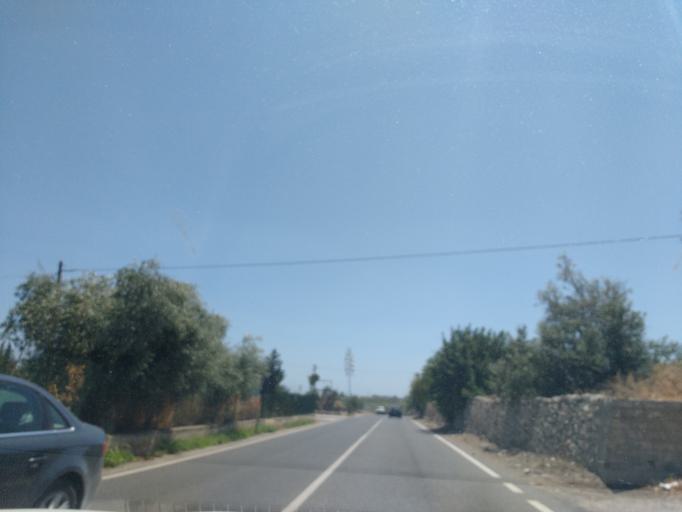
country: IT
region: Sicily
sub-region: Provincia di Siracusa
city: Noto
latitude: 36.8775
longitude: 15.0472
